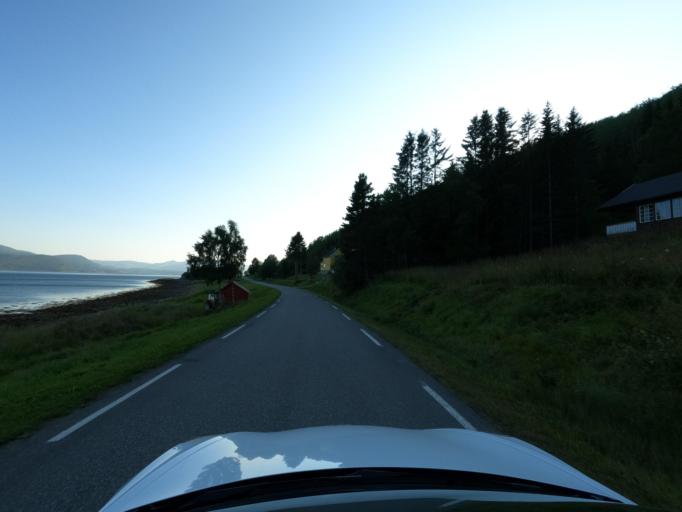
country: NO
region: Nordland
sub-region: Ballangen
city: Ballangen
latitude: 68.4670
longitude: 16.7859
